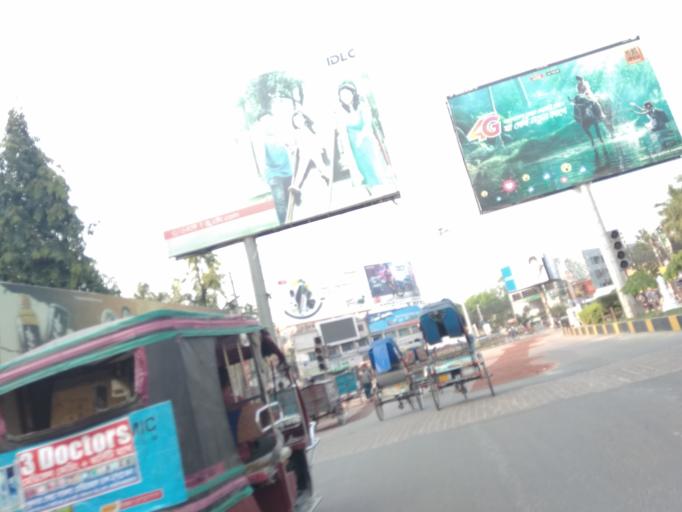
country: BD
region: Khulna
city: Khulna
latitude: 22.8216
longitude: 89.5529
